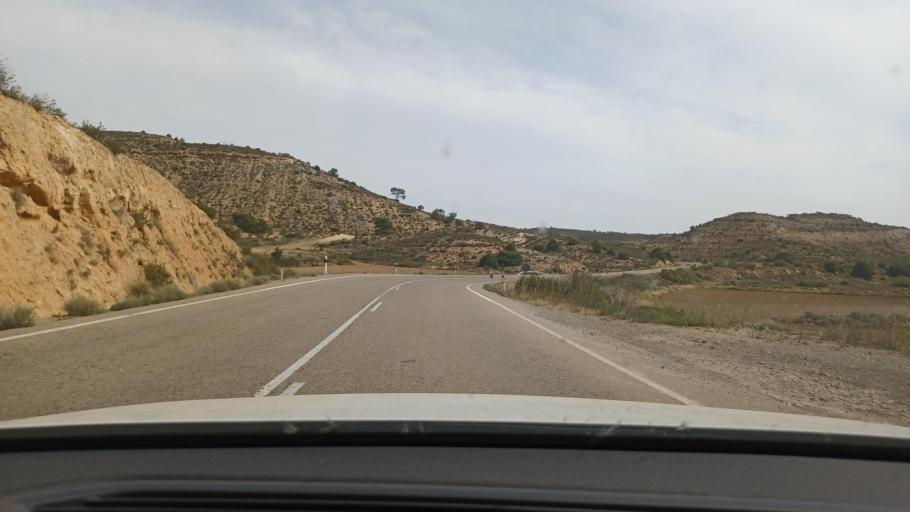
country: ES
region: Aragon
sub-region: Provincia de Zaragoza
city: Chiprana
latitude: 41.3413
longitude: -0.0887
